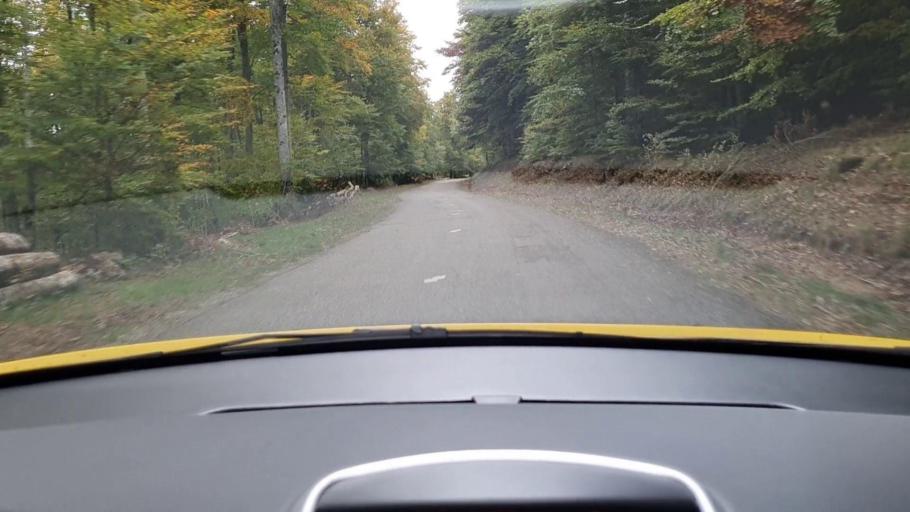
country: FR
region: Languedoc-Roussillon
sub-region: Departement de la Lozere
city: Meyrueis
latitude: 44.0941
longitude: 3.4604
